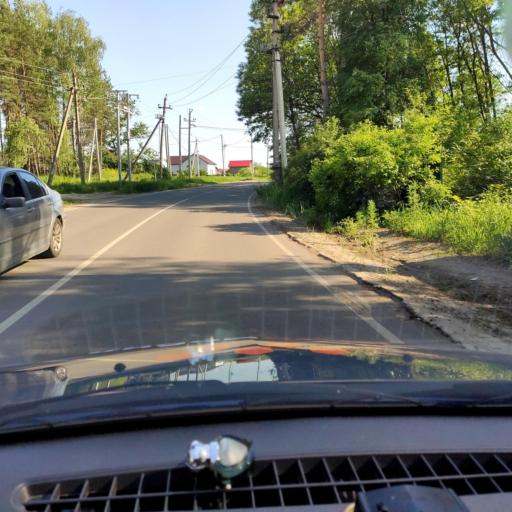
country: RU
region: Voronezj
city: Podgornoye
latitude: 51.8211
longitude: 39.1428
